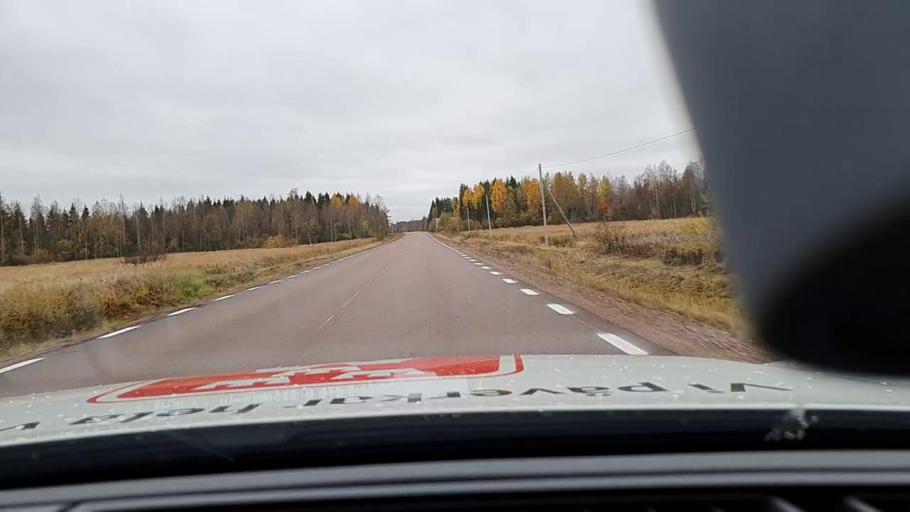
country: FI
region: Lapland
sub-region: Kemi-Tornio
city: Tornio
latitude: 66.0818
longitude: 23.9242
